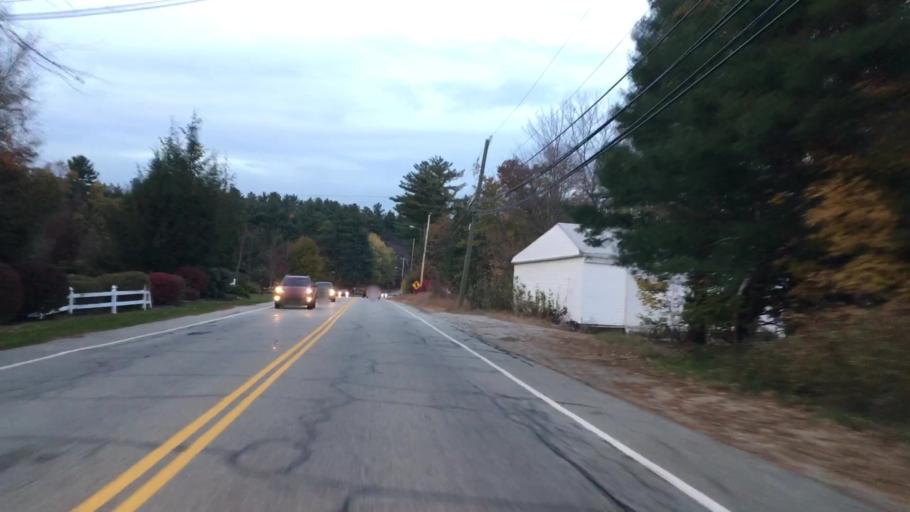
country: US
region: New Hampshire
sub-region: Hillsborough County
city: Milford
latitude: 42.8418
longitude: -71.6381
